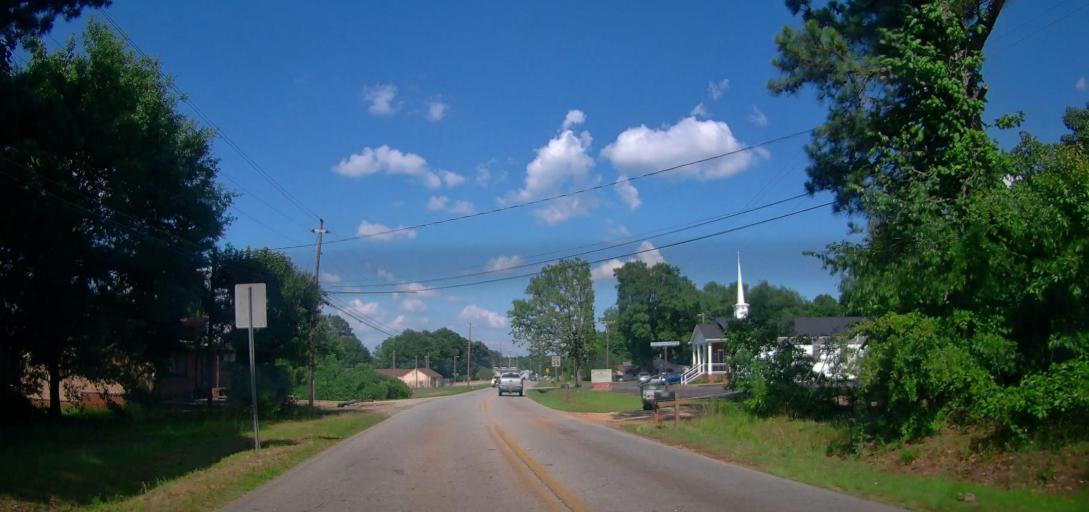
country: US
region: Georgia
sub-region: Spalding County
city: Experiment
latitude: 33.2792
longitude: -84.2671
